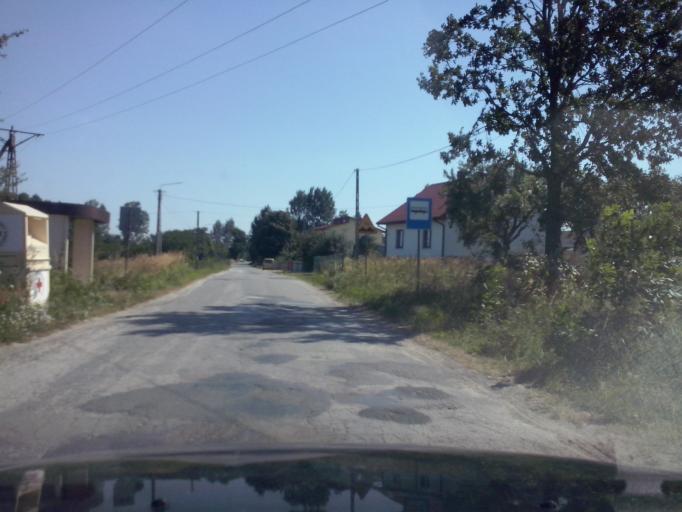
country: PL
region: Swietokrzyskie
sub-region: Powiat kielecki
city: Chmielnik
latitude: 50.6023
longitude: 20.7978
